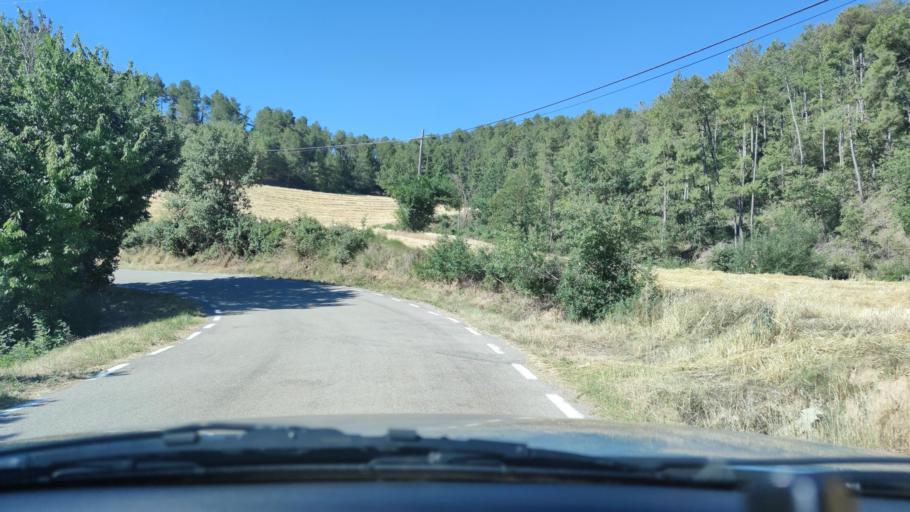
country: ES
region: Catalonia
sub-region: Provincia de Lleida
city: Solsona
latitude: 41.9562
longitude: 1.4922
